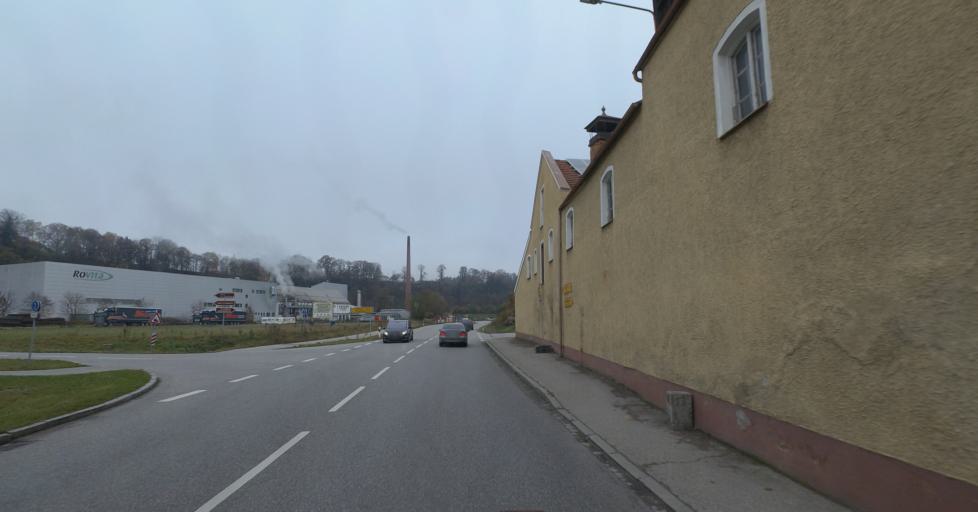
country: DE
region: Bavaria
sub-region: Upper Bavaria
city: Engelsberg
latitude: 48.1060
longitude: 12.5658
